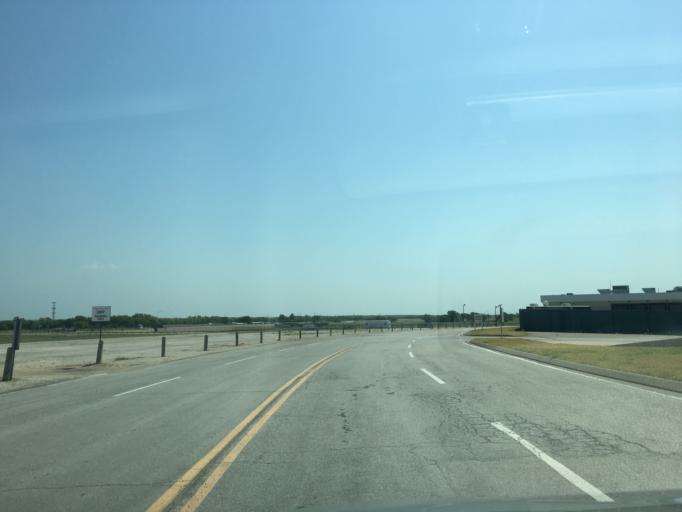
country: US
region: Texas
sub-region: Denton County
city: Justin
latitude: 33.0425
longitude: -97.2817
